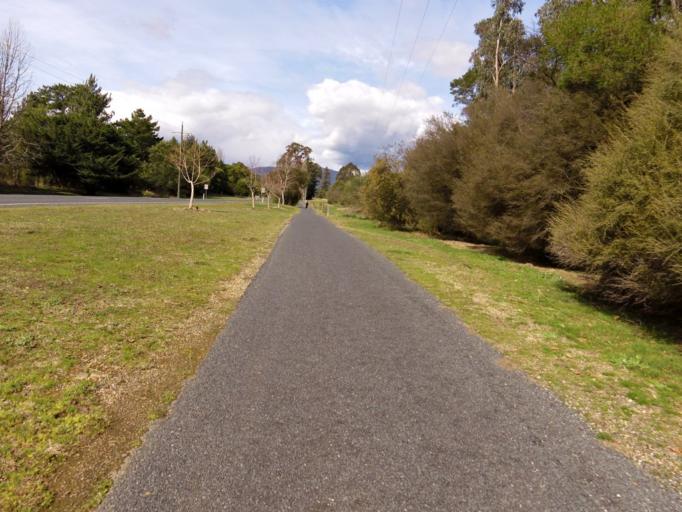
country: AU
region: Victoria
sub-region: Alpine
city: Mount Beauty
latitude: -36.7052
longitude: 146.9273
